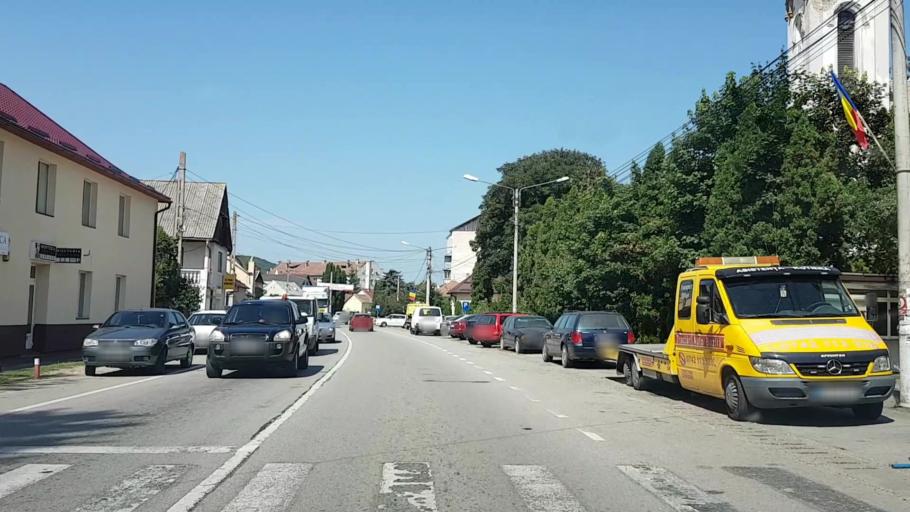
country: RO
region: Bistrita-Nasaud
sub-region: Comuna Beclean
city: Beclean
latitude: 47.1807
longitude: 24.1811
